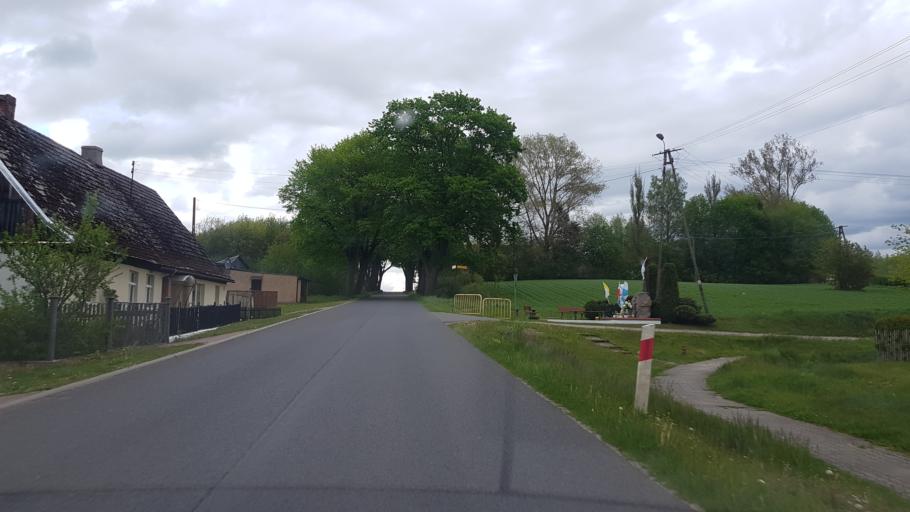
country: PL
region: West Pomeranian Voivodeship
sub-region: Powiat slawienski
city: Slawno
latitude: 54.2728
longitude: 16.5311
